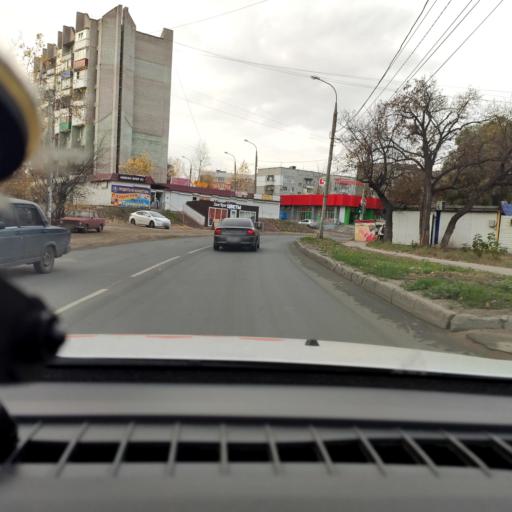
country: RU
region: Samara
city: Rozhdestveno
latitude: 53.1441
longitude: 50.0501
